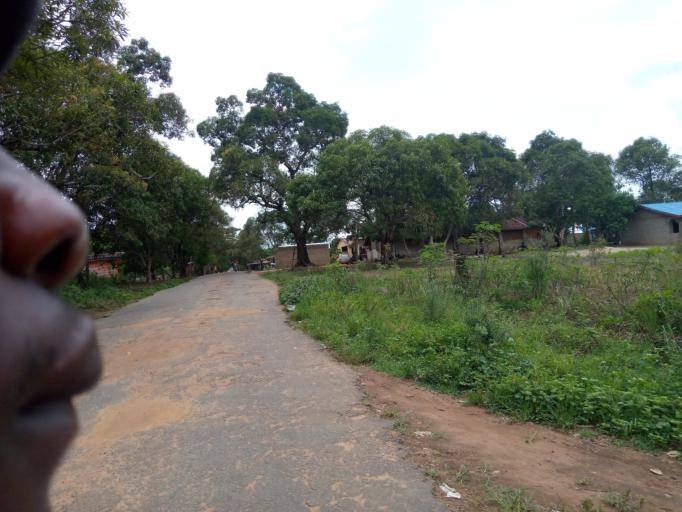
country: SL
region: Western Area
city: Waterloo
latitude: 8.3347
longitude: -13.0007
